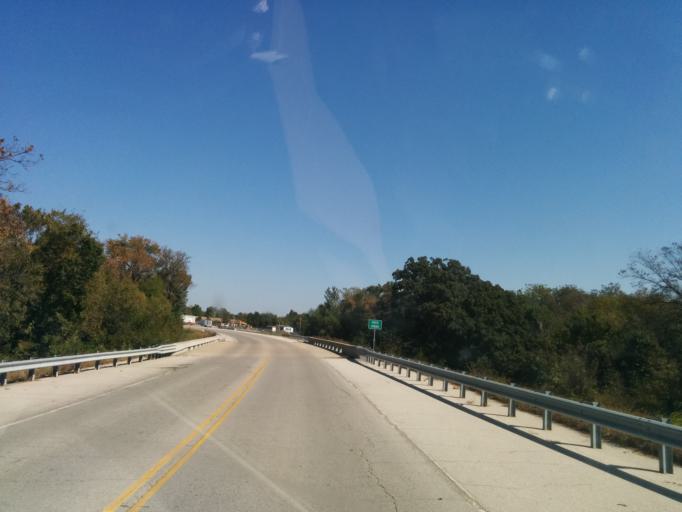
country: US
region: Oklahoma
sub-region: Creek County
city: Mounds
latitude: 35.8660
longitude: -96.0625
